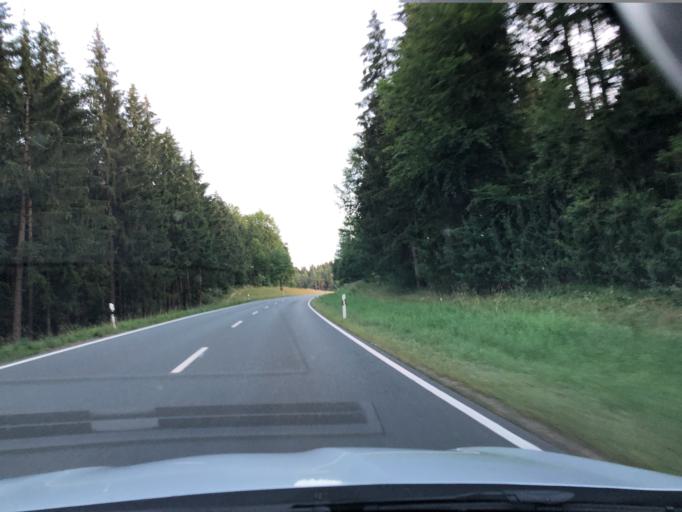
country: DE
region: Bavaria
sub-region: Upper Palatinate
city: Illschwang
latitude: 49.4357
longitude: 11.6589
